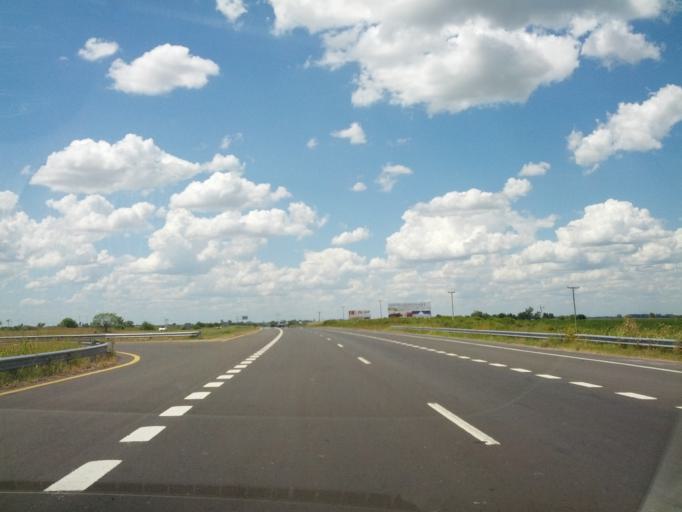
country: AR
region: Entre Rios
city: Colonia Elia
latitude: -32.5799
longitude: -58.3891
